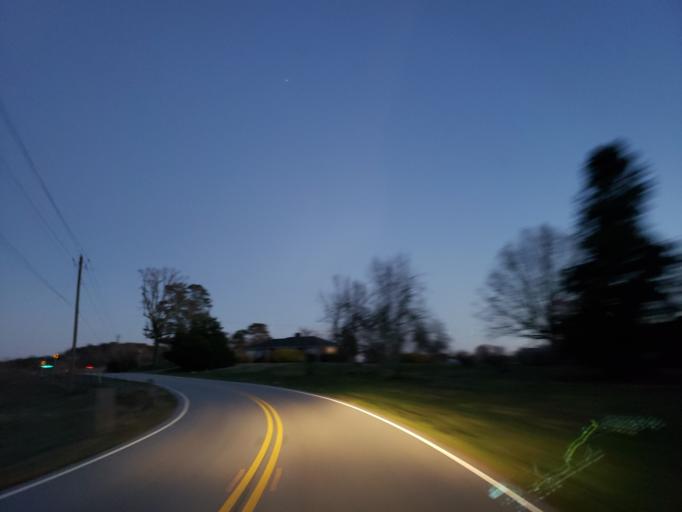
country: US
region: Georgia
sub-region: Bartow County
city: Emerson
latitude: 34.0649
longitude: -84.8130
